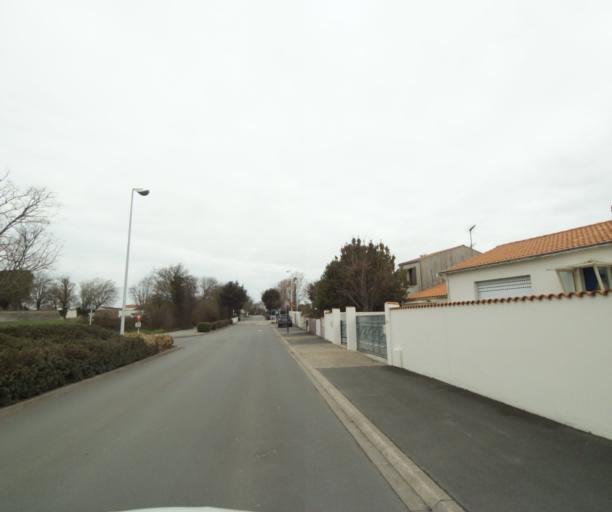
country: FR
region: Poitou-Charentes
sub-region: Departement de la Charente-Maritime
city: Lagord
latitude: 46.1897
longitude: -1.1581
